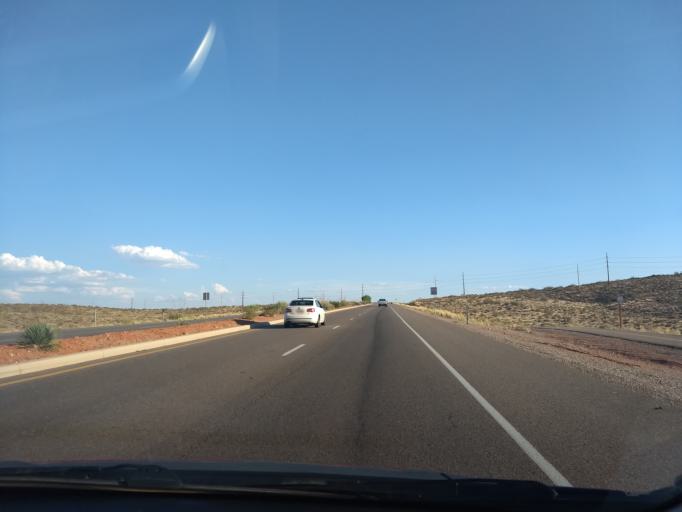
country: US
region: Utah
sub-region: Washington County
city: Saint George
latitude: 37.1298
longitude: -113.5829
